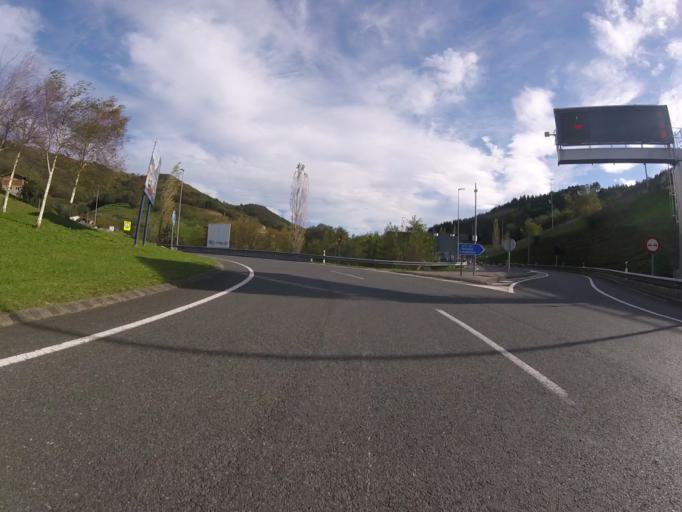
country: ES
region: Basque Country
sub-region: Provincia de Guipuzcoa
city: Orio
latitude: 43.2820
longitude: -2.1119
